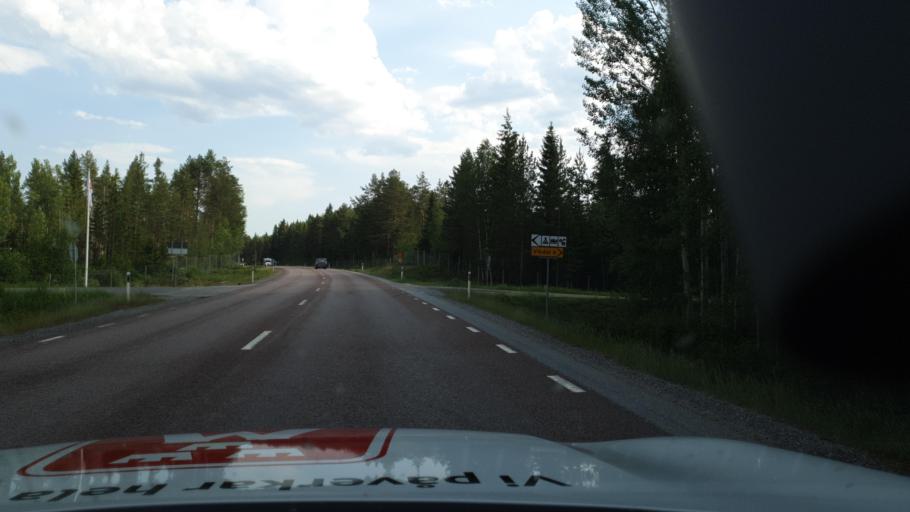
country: SE
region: Vaesterbotten
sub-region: Skelleftea Kommun
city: Burea
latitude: 64.6165
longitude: 21.1794
